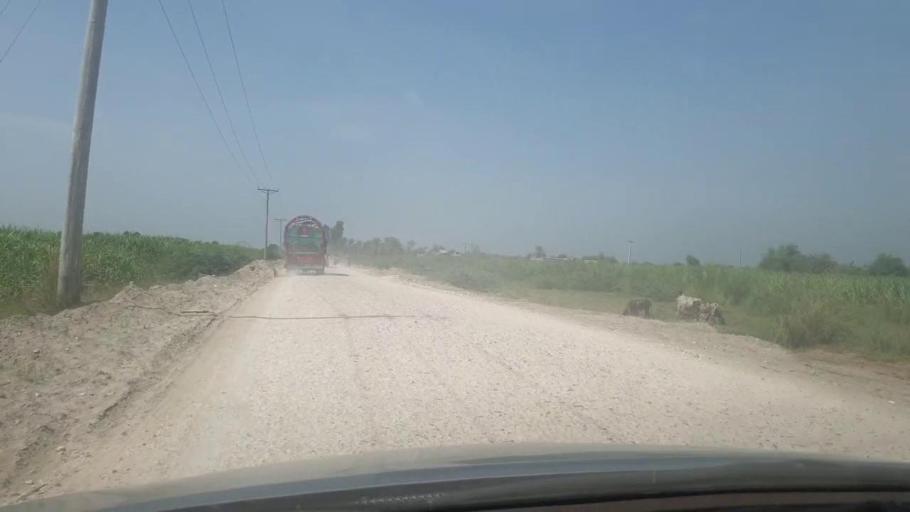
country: PK
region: Sindh
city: Ranipur
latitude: 27.2799
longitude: 68.6001
